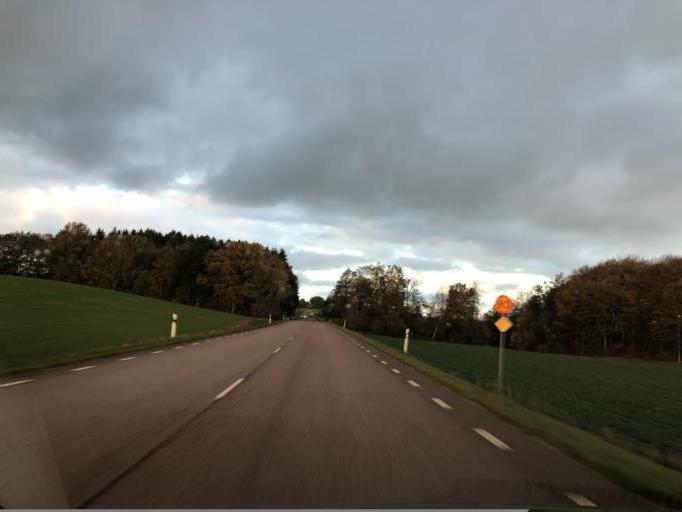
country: SE
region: Skane
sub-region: Klippans Kommun
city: Ljungbyhed
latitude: 55.9793
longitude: 13.2691
